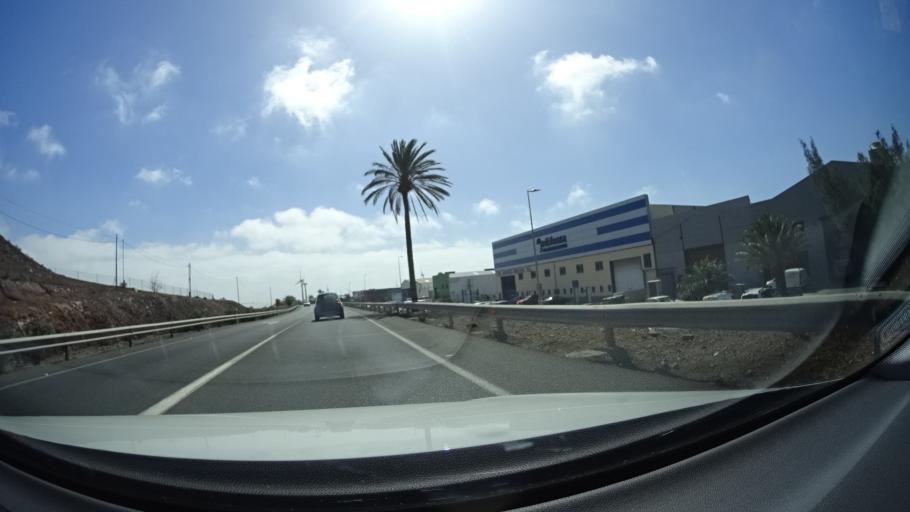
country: ES
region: Canary Islands
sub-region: Provincia de Las Palmas
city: Cruce de Arinaga
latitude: 27.8676
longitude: -15.4142
